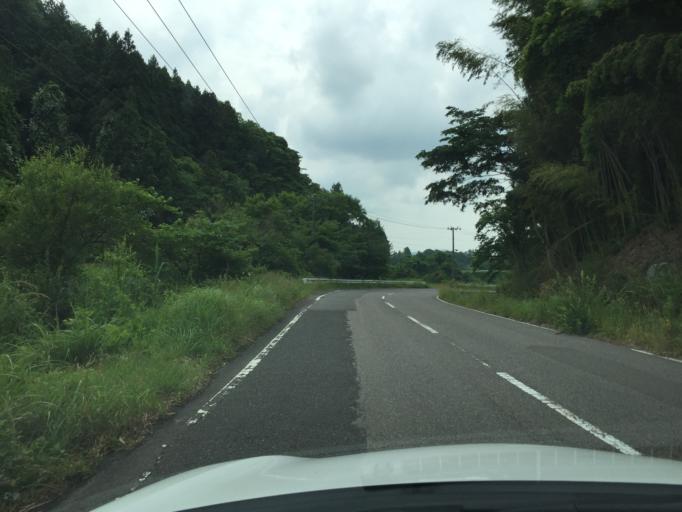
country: JP
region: Fukushima
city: Funehikimachi-funehiki
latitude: 37.3045
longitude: 140.5531
